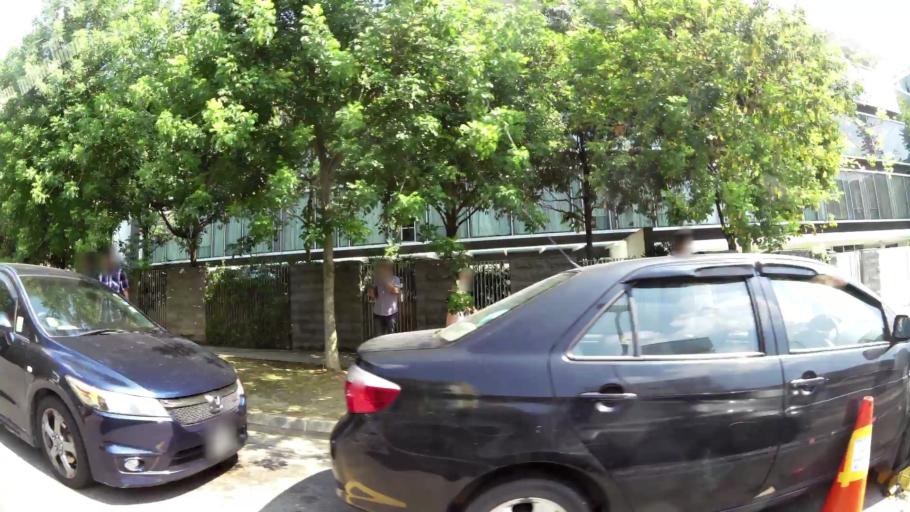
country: SG
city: Singapore
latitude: 1.3032
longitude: 103.8472
